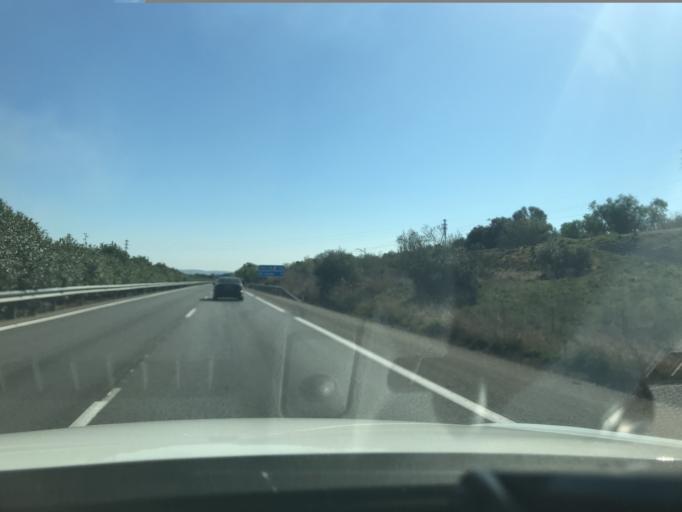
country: ES
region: Andalusia
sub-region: Province of Cordoba
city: Villafranca de Cordoba
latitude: 37.9521
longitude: -4.5298
